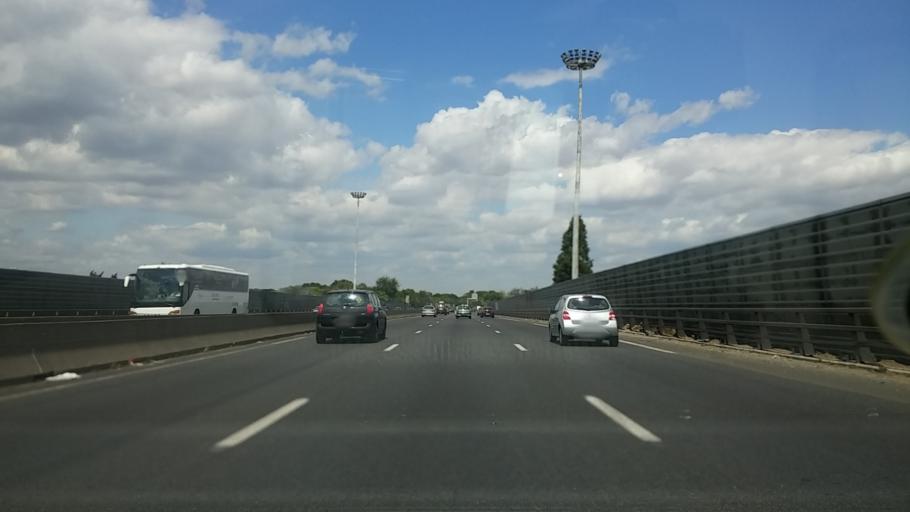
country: FR
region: Ile-de-France
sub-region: Departement de Seine-Saint-Denis
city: Noisy-le-Sec
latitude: 48.9043
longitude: 2.4719
